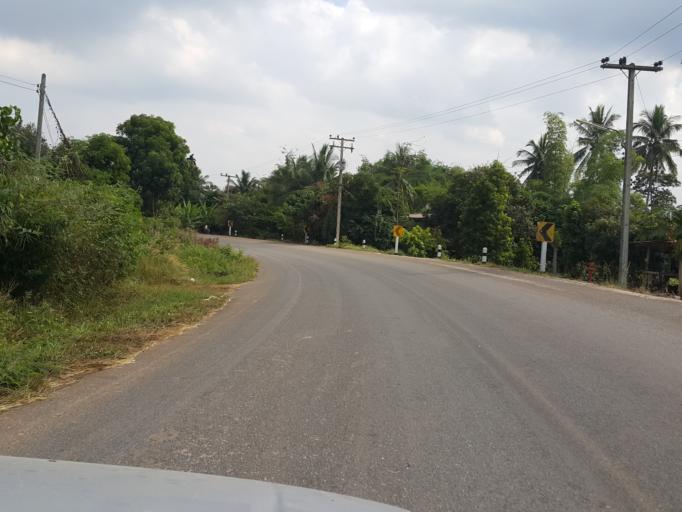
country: TH
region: Sukhothai
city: Thung Saliam
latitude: 17.4494
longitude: 99.6066
